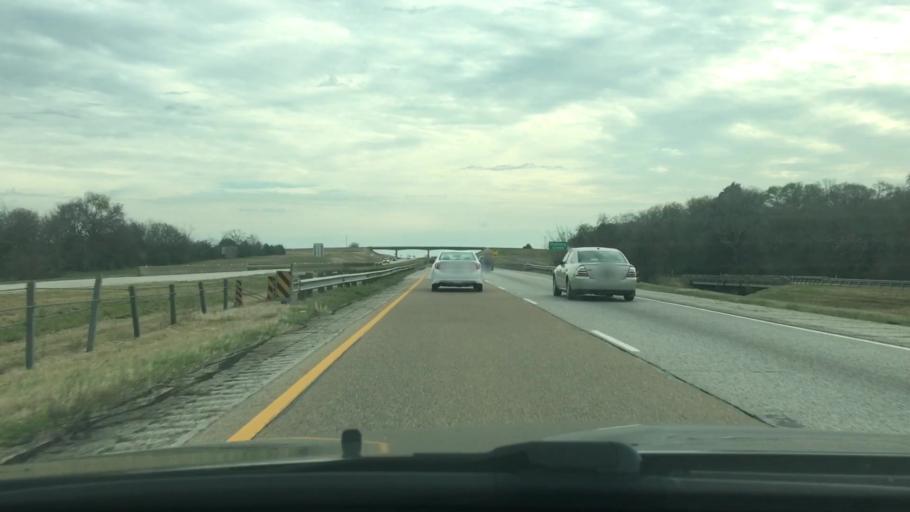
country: US
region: Texas
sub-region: Leon County
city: Centerville
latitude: 31.1290
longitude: -95.9776
